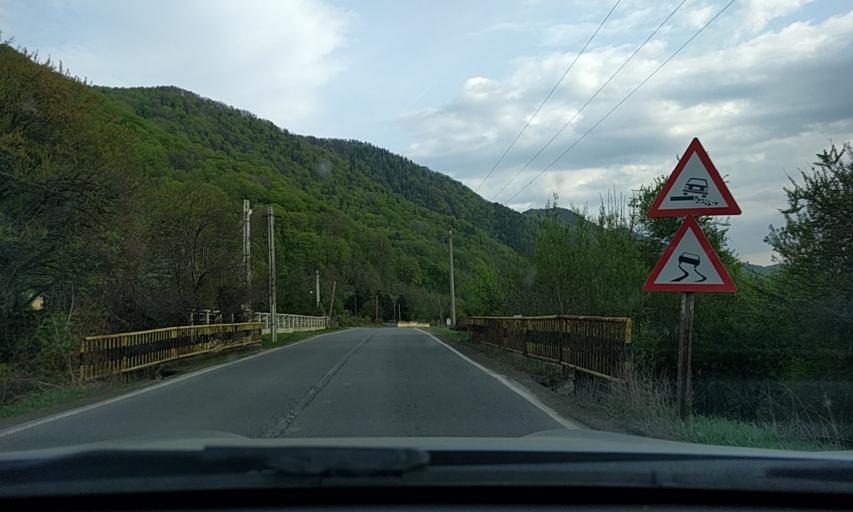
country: RO
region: Bacau
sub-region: Oras Slanic-Moldova
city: Slanic-Moldova
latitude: 46.1501
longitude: 26.4593
